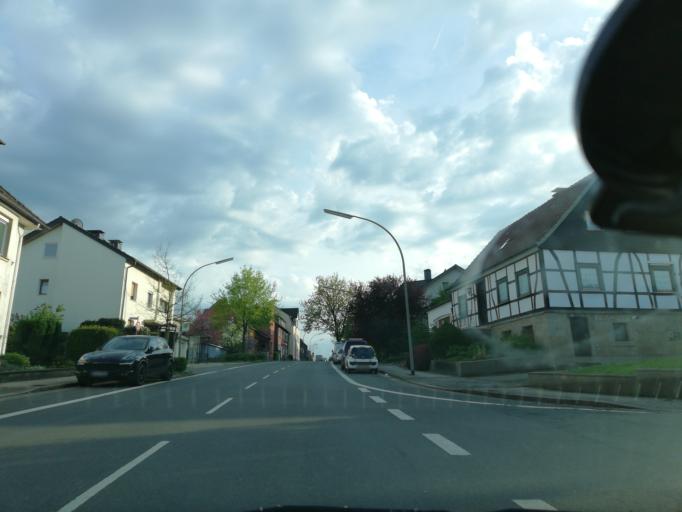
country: DE
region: North Rhine-Westphalia
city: Wetter (Ruhr)
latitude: 51.3768
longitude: 7.3726
